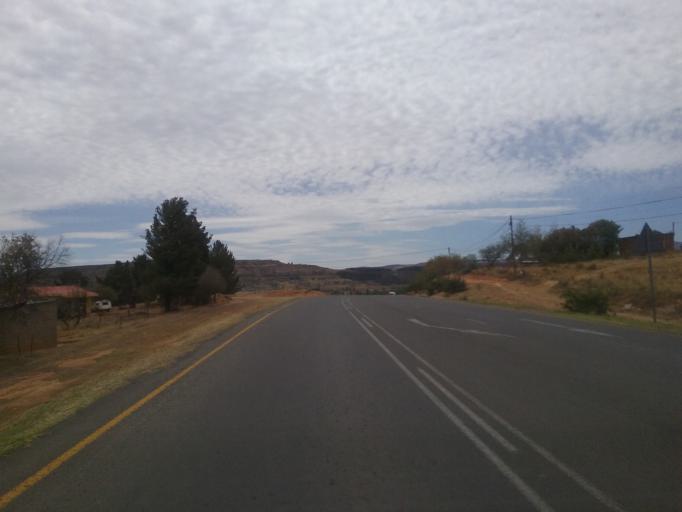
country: LS
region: Maseru
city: Nako
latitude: -29.6272
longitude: 27.4873
